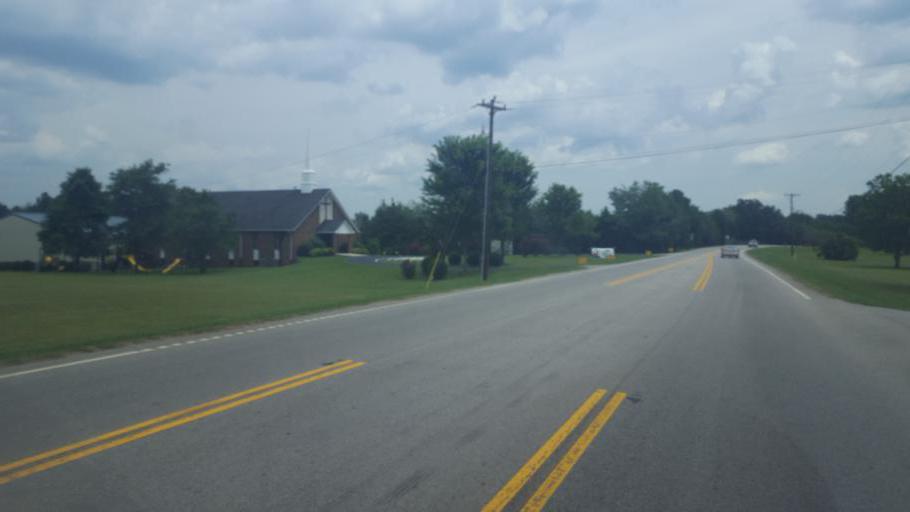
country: US
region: South Carolina
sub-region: York County
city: York
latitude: 34.9820
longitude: -81.1946
